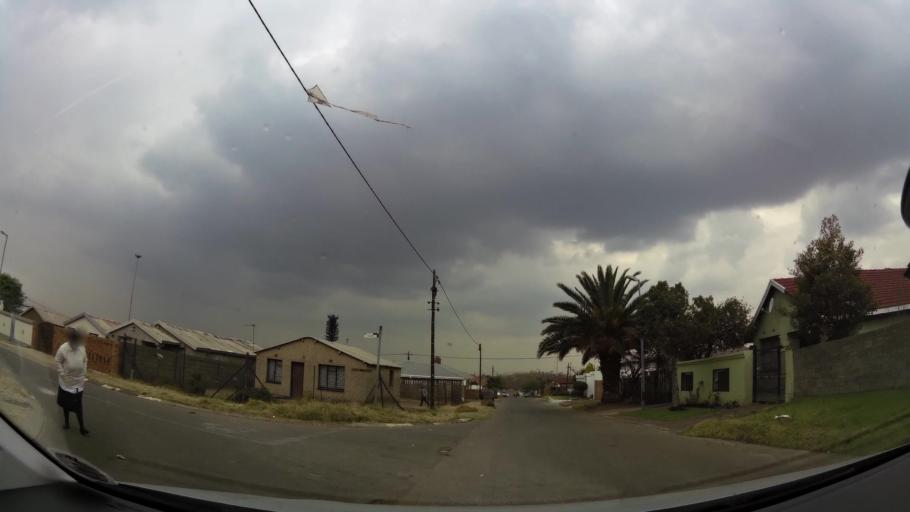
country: ZA
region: Gauteng
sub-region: City of Johannesburg Metropolitan Municipality
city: Soweto
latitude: -26.2598
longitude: 27.8673
